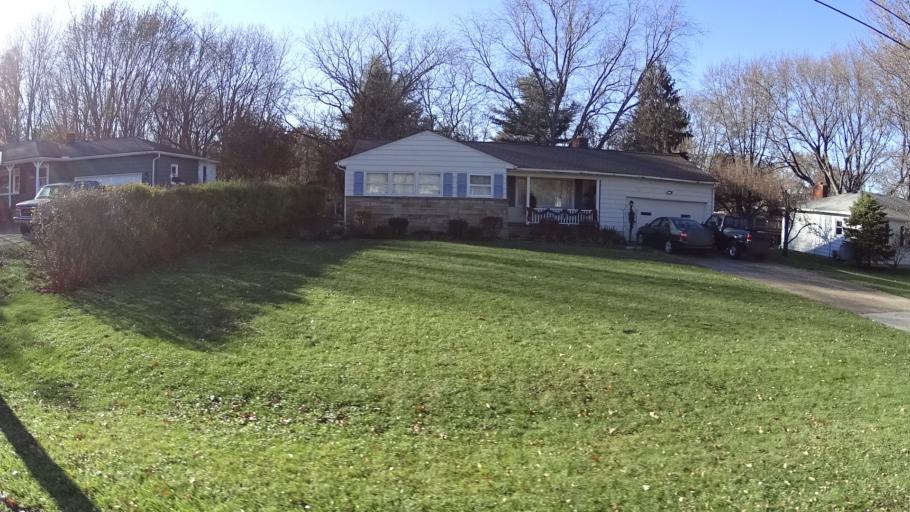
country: US
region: Ohio
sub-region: Lorain County
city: Avon Center
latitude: 41.4521
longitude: -81.9938
